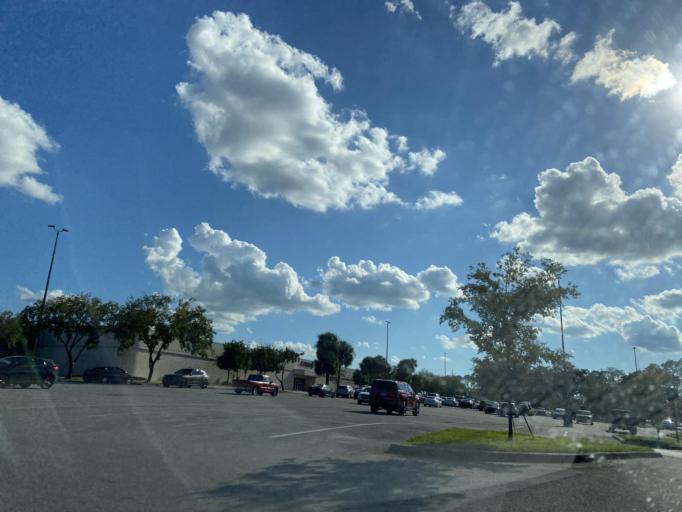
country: US
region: Florida
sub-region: Marion County
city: Ocala
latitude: 29.1608
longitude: -82.1735
